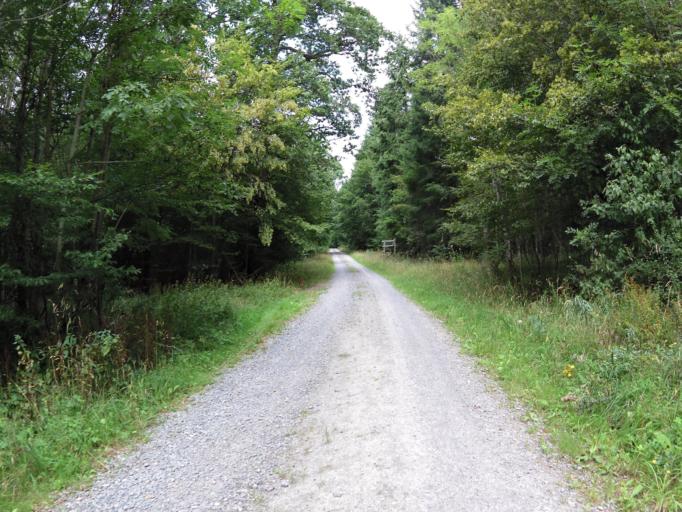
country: DE
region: Bavaria
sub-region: Regierungsbezirk Unterfranken
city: Kleinrinderfeld
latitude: 49.7164
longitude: 9.8156
